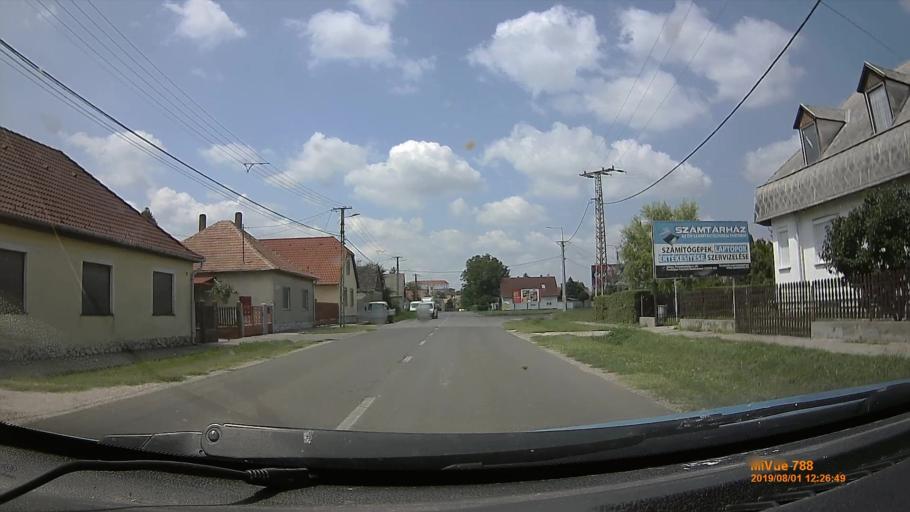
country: HU
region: Baranya
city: Siklos
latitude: 45.8522
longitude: 18.3084
